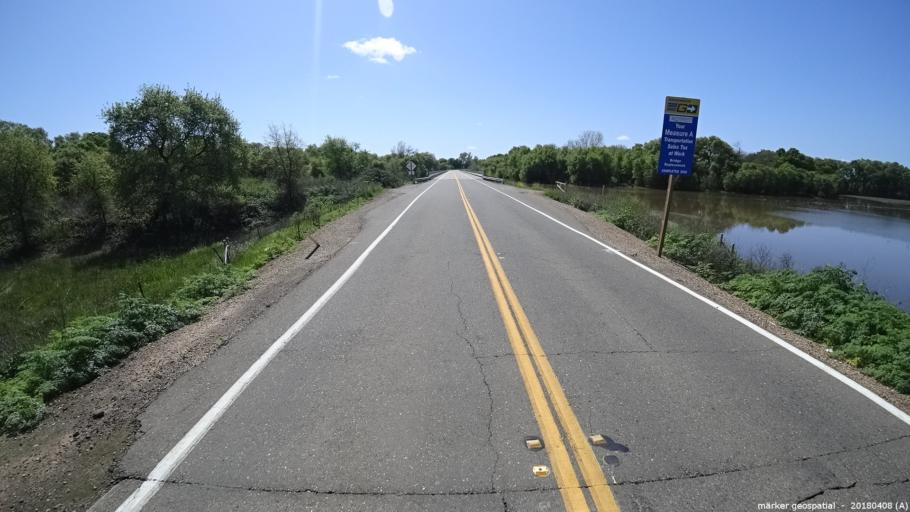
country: US
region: California
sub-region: San Joaquin County
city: Thornton
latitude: 38.2615
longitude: -121.4406
